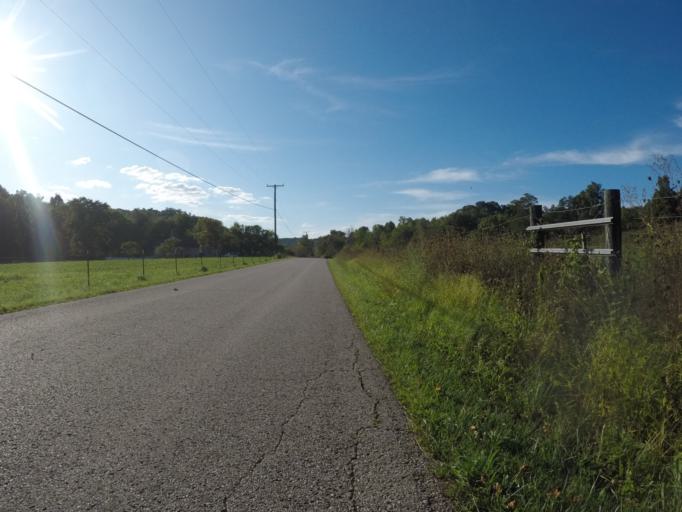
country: US
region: West Virginia
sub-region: Cabell County
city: Huntington
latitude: 38.5074
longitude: -82.4913
